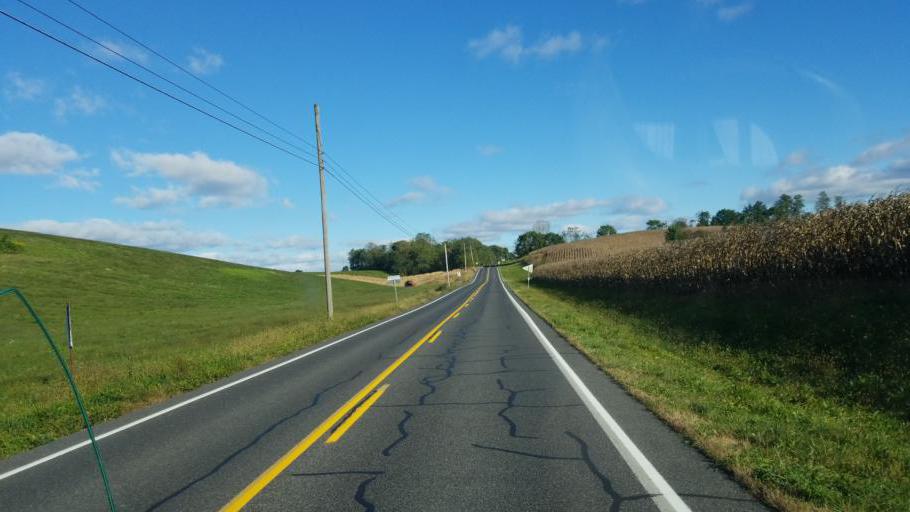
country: US
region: Pennsylvania
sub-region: Franklin County
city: Mont Alto
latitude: 39.8491
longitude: -77.5596
